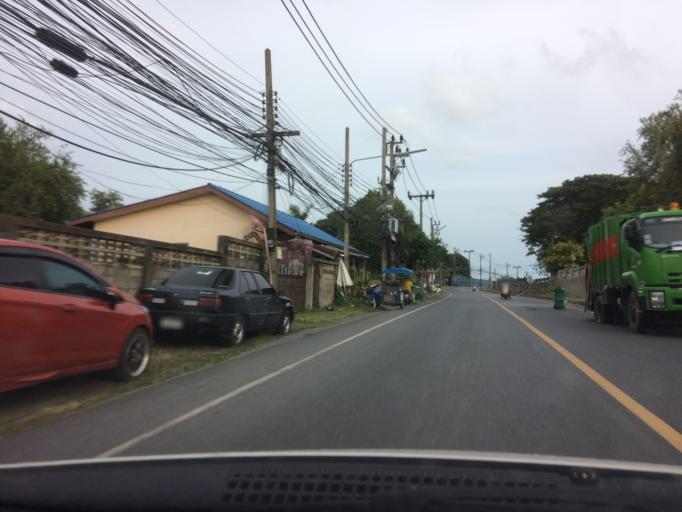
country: TH
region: Phuket
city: Ban Ratsada
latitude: 7.9039
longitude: 98.4097
